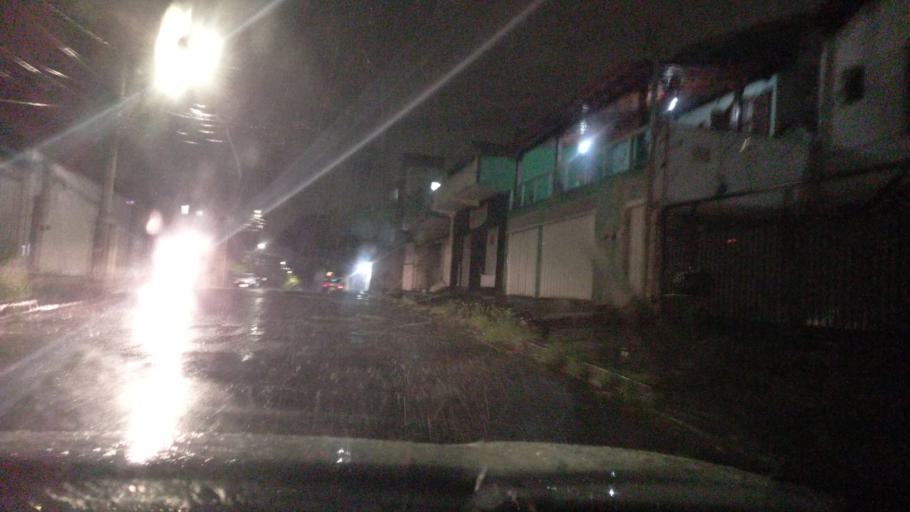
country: BR
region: Minas Gerais
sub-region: Belo Horizonte
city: Belo Horizonte
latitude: -19.9056
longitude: -43.9766
